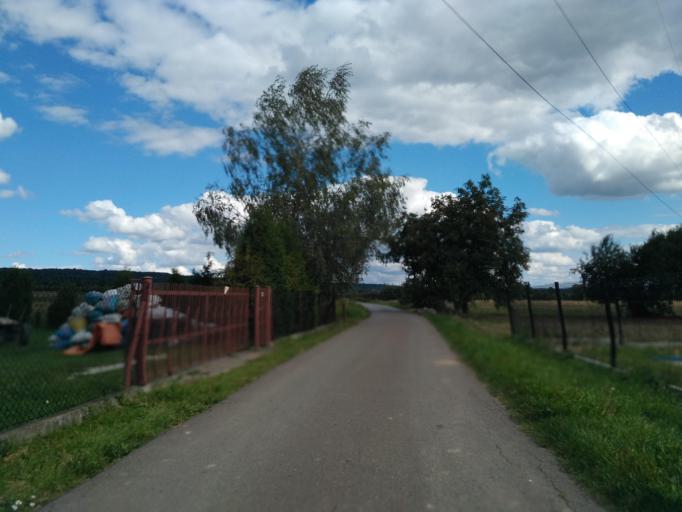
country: PL
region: Subcarpathian Voivodeship
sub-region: Powiat jasielski
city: Jaslo
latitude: 49.7611
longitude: 21.5081
